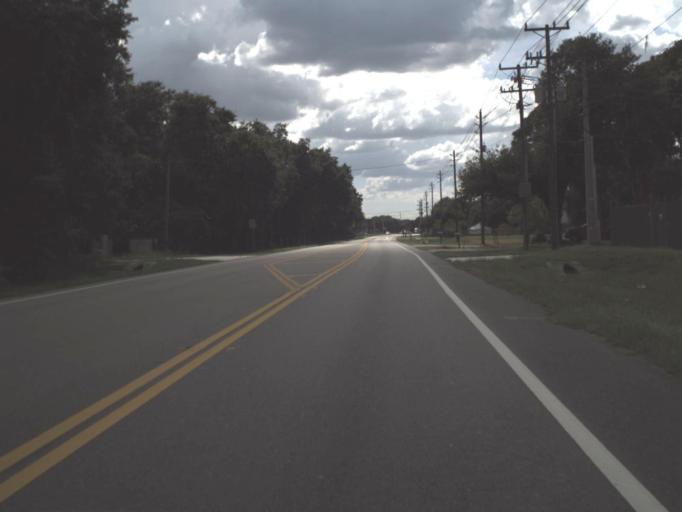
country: US
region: Florida
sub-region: Polk County
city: Winston
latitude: 28.0287
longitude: -82.0503
